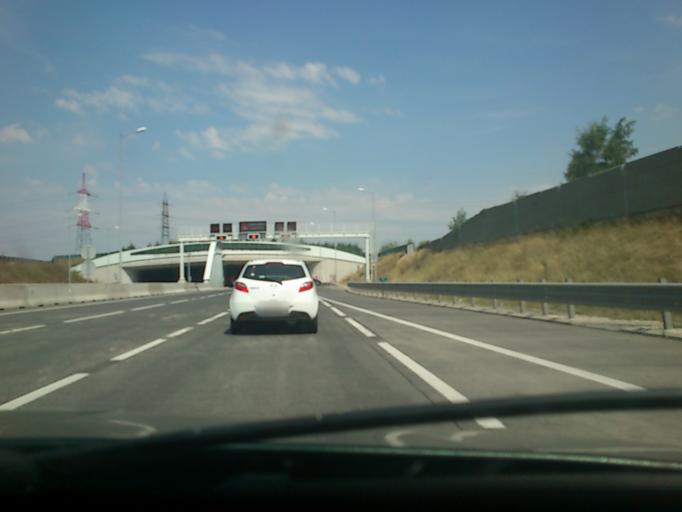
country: AT
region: Lower Austria
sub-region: Politischer Bezirk Mistelbach
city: Grossebersdorf
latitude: 48.3565
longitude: 16.4837
